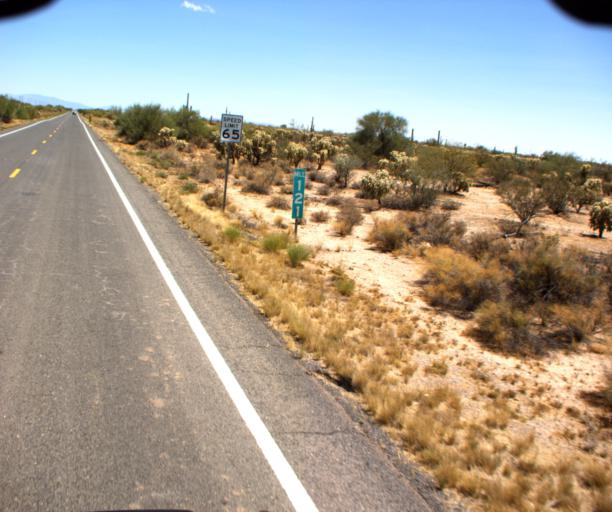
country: US
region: Arizona
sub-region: Pinal County
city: Florence
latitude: 32.8833
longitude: -111.2620
